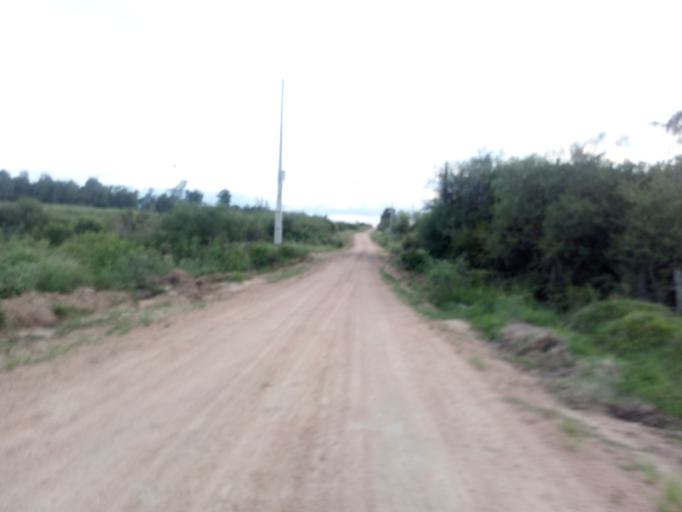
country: BR
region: Rio Grande do Sul
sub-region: Sao Gabriel
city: Sao Gabriel
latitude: -30.3233
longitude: -54.3504
